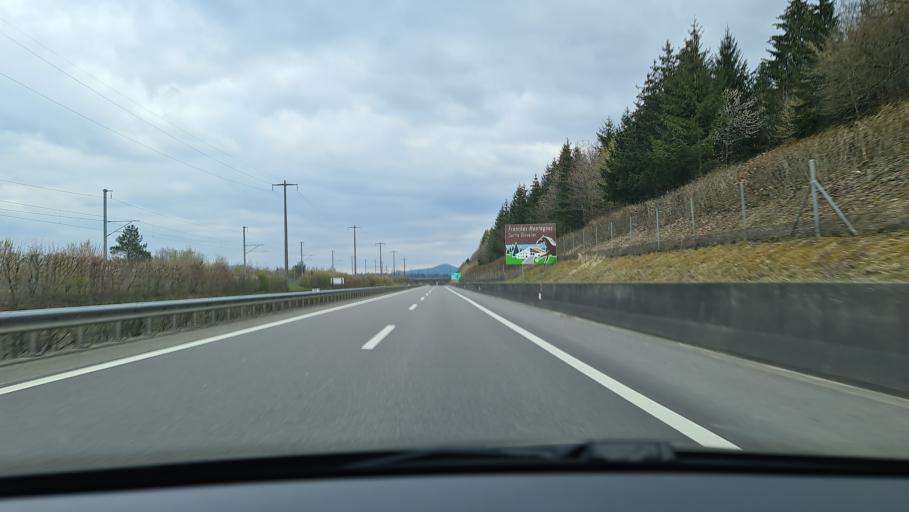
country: CH
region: Jura
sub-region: Porrentruy District
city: Courgenay
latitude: 47.4176
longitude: 7.1111
